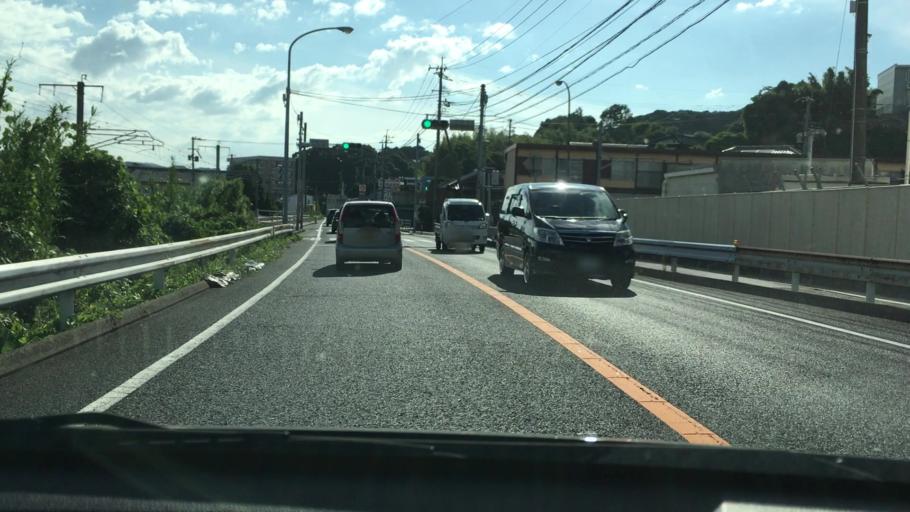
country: JP
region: Nagasaki
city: Sasebo
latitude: 33.1450
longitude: 129.8055
